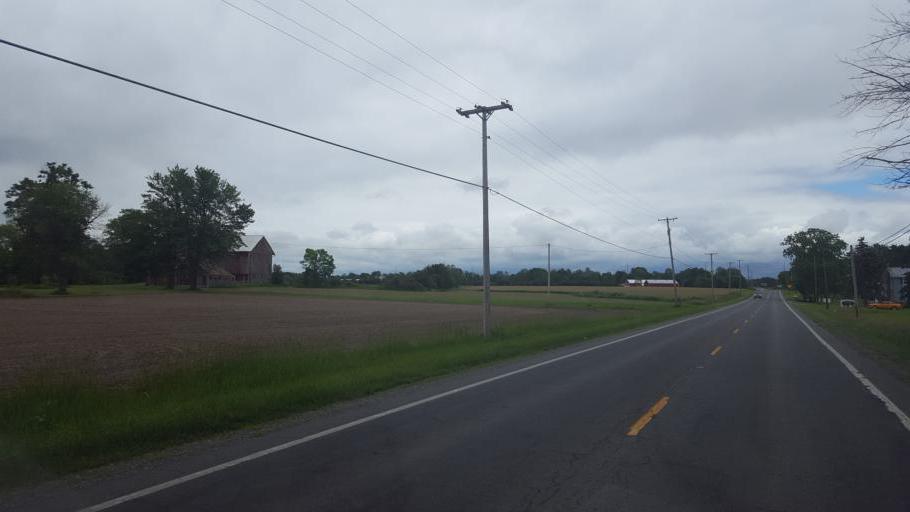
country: US
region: Ohio
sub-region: Crawford County
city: Galion
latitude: 40.7420
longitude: -82.8352
